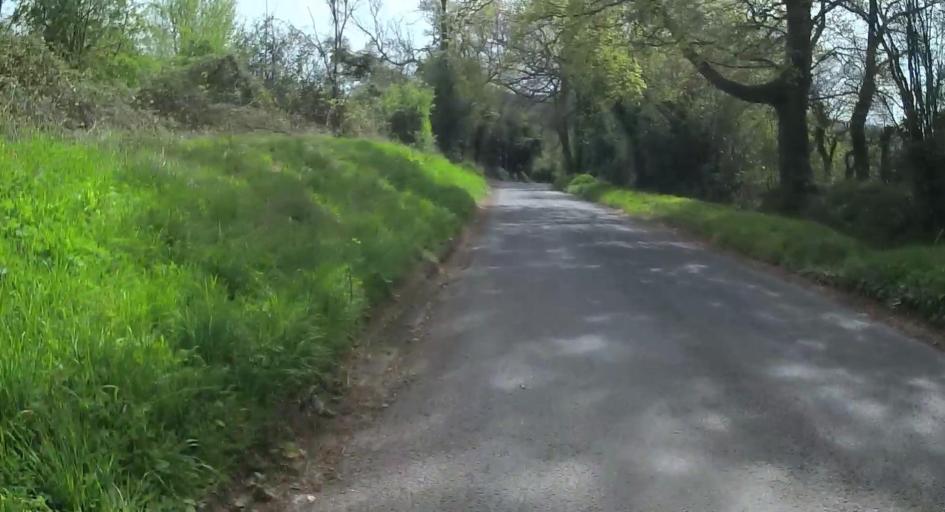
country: GB
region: England
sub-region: Hampshire
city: Alton
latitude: 51.1728
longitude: -0.9607
